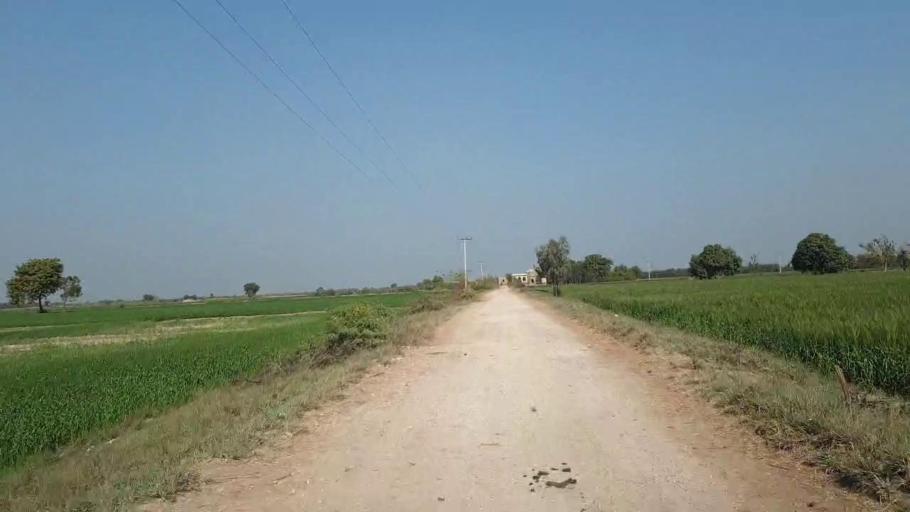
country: PK
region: Sindh
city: Hala
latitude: 25.9177
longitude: 68.4298
